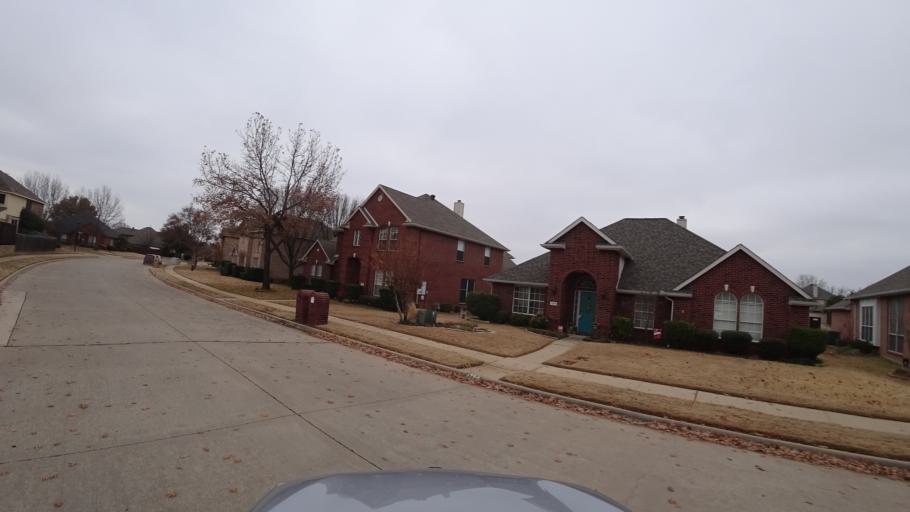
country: US
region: Texas
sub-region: Denton County
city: Lewisville
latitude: 33.0568
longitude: -97.0279
